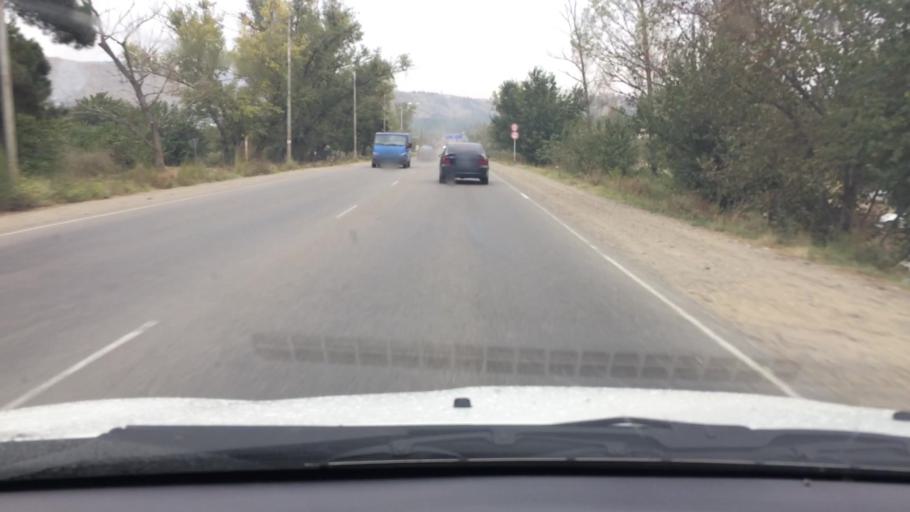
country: GE
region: T'bilisi
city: Tbilisi
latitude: 41.6096
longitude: 44.7858
